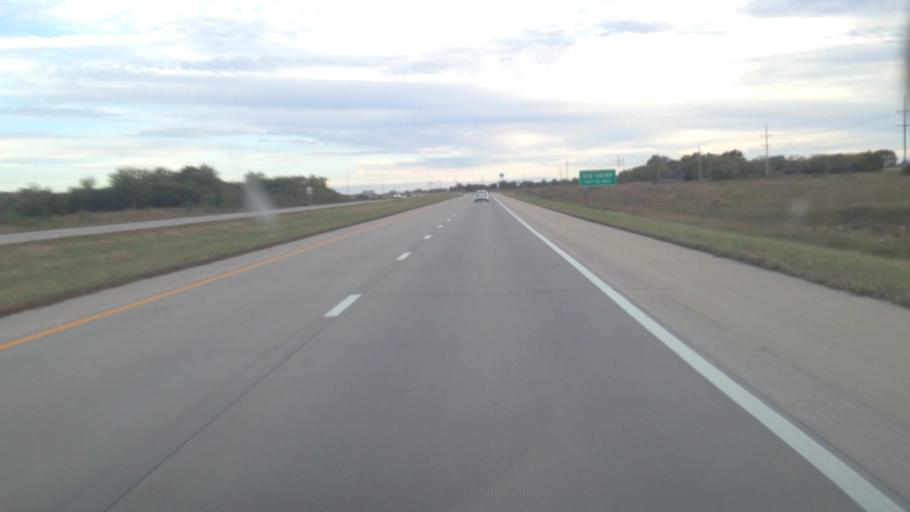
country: US
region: Kansas
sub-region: Franklin County
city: Ottawa
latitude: 38.7014
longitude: -95.2685
